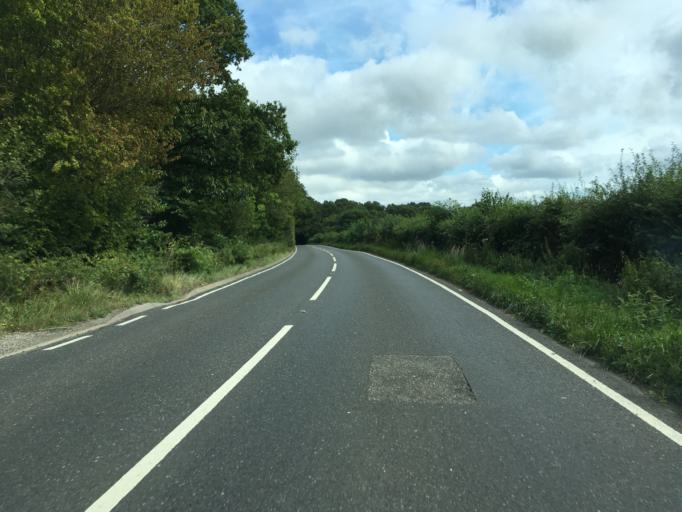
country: GB
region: England
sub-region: Kent
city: Paddock Wood
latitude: 51.1105
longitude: 0.4103
